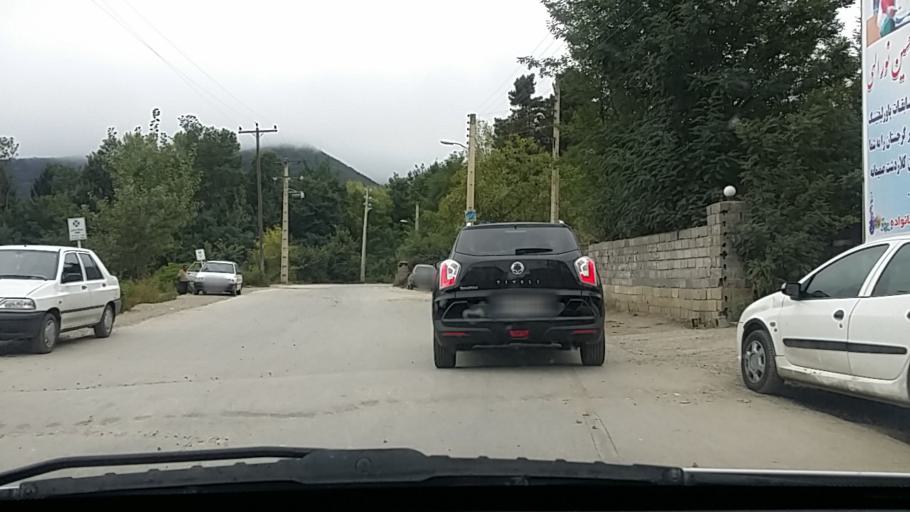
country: IR
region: Mazandaran
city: `Abbasabad
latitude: 36.5048
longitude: 51.1609
